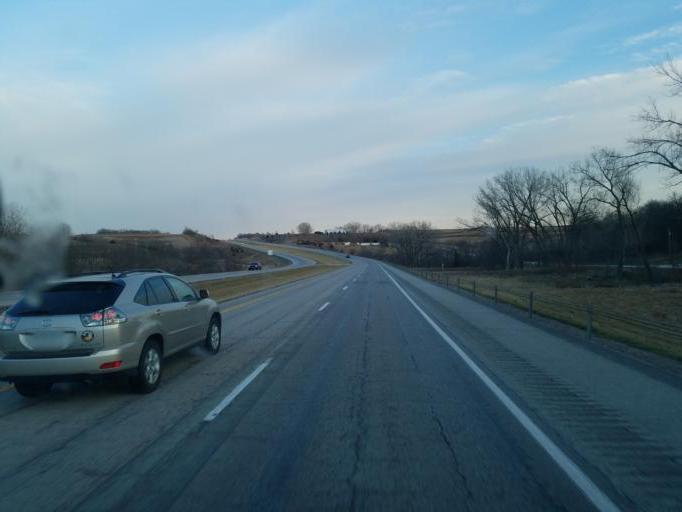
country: US
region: Iowa
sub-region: Harrison County
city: Missouri Valley
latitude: 41.4938
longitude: -95.8580
